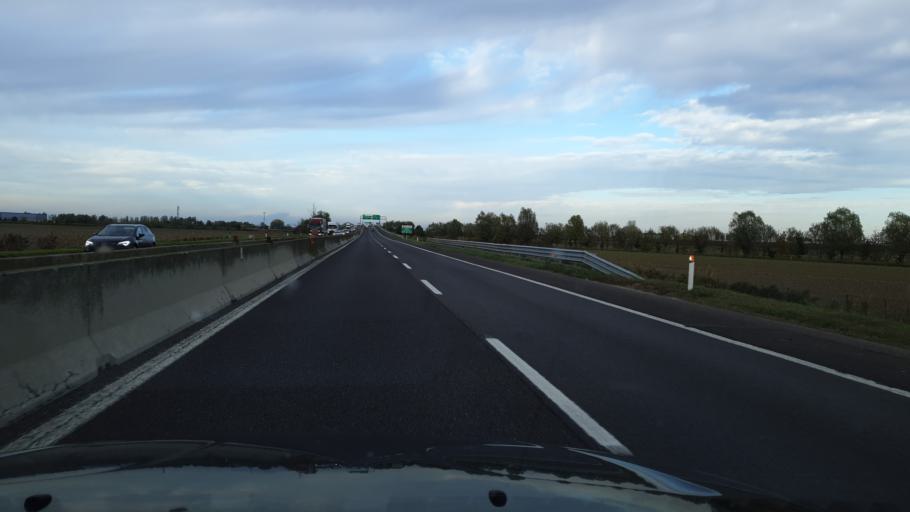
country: IT
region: Veneto
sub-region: Provincia di Padova
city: Boara Pisani
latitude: 45.1070
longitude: 11.7576
